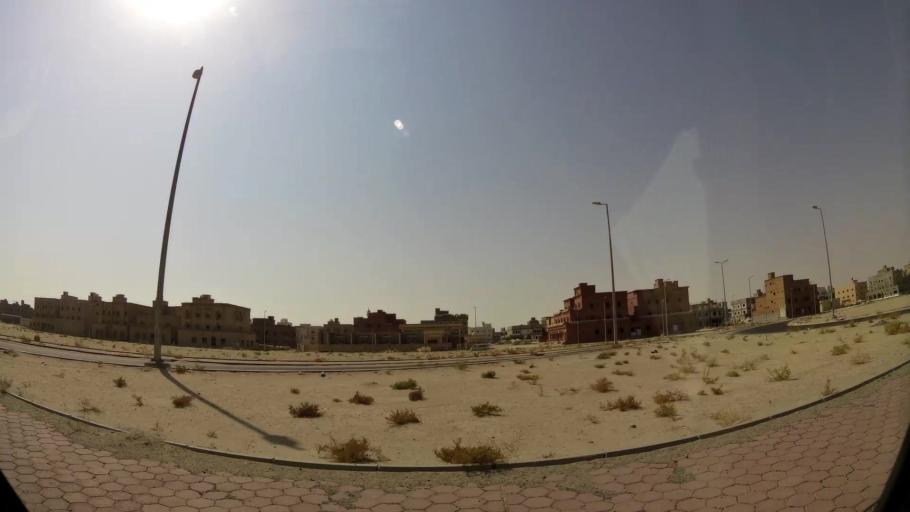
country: KW
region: Al Ahmadi
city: Al Wafrah
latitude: 28.8004
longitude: 48.0540
